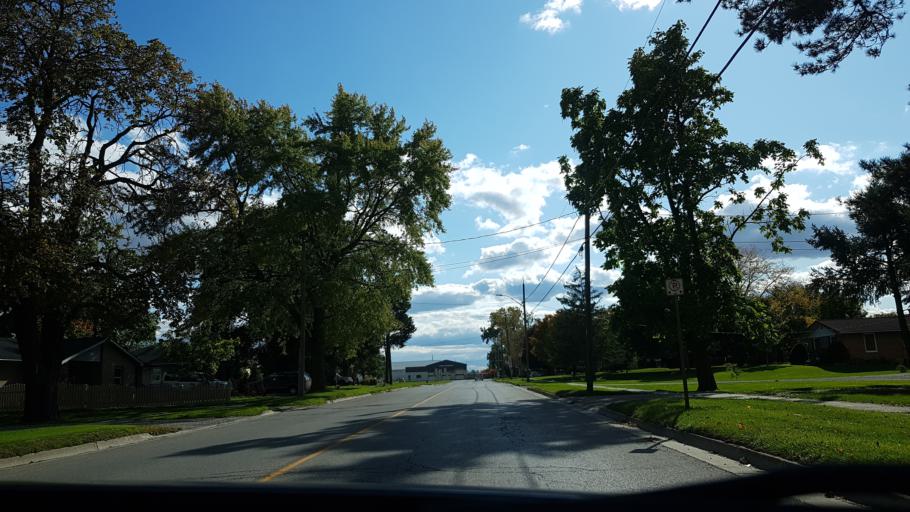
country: CA
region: Ontario
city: South Huron
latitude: 43.1554
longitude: -81.6863
